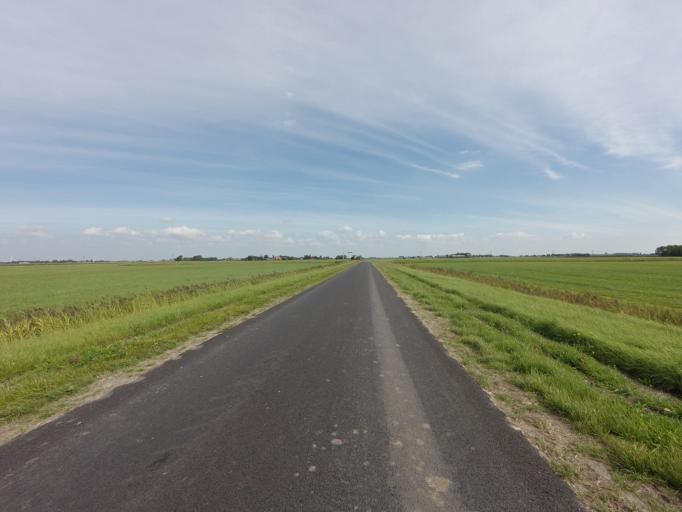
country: NL
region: Friesland
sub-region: Gemeente Franekeradeel
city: Sexbierum
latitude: 53.1641
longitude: 5.4840
